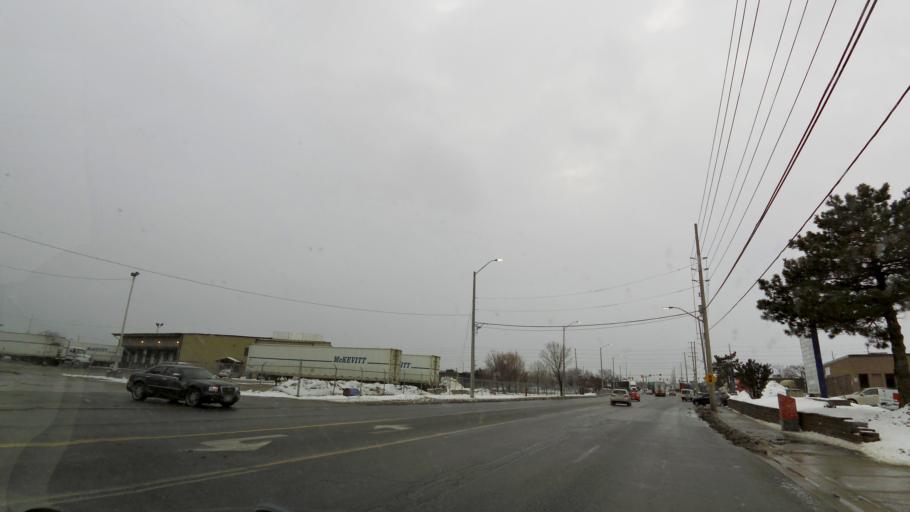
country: CA
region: Ontario
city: Etobicoke
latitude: 43.6571
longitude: -79.6458
